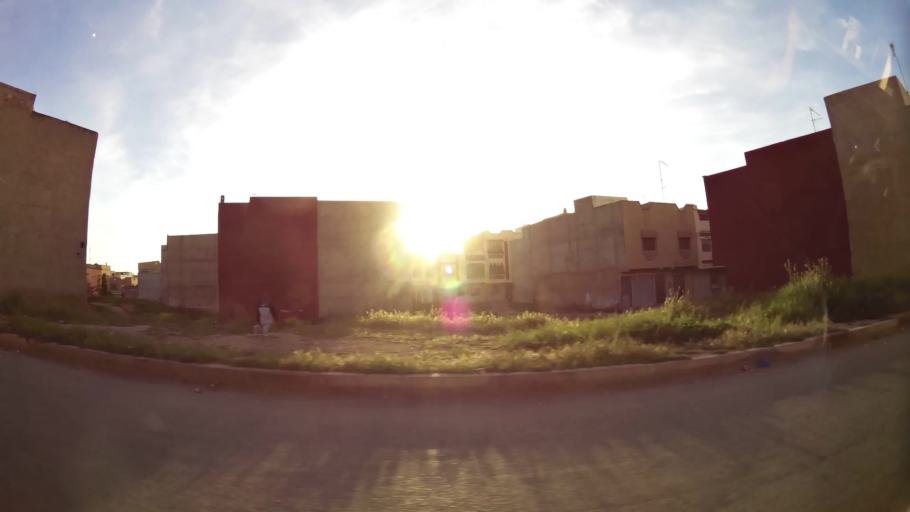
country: MA
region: Oriental
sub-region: Oujda-Angad
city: Oujda
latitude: 34.6768
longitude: -1.8968
